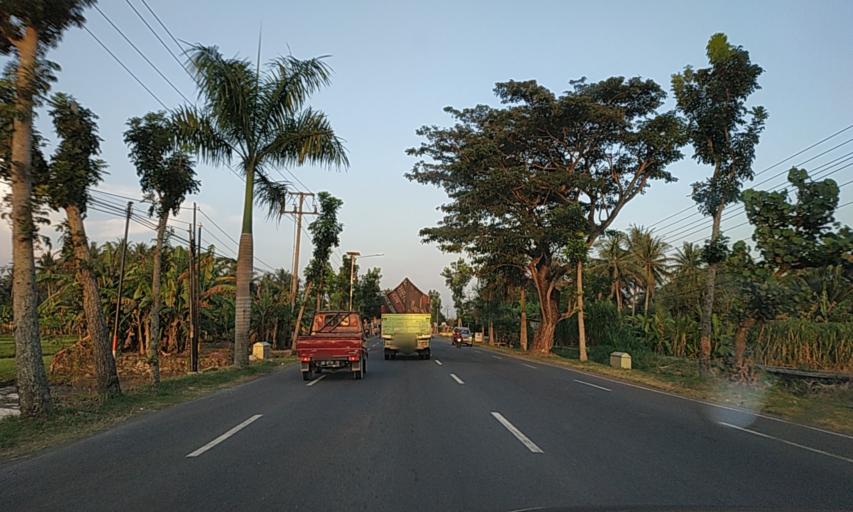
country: ID
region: Daerah Istimewa Yogyakarta
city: Srandakan
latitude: -7.8886
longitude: 110.0960
